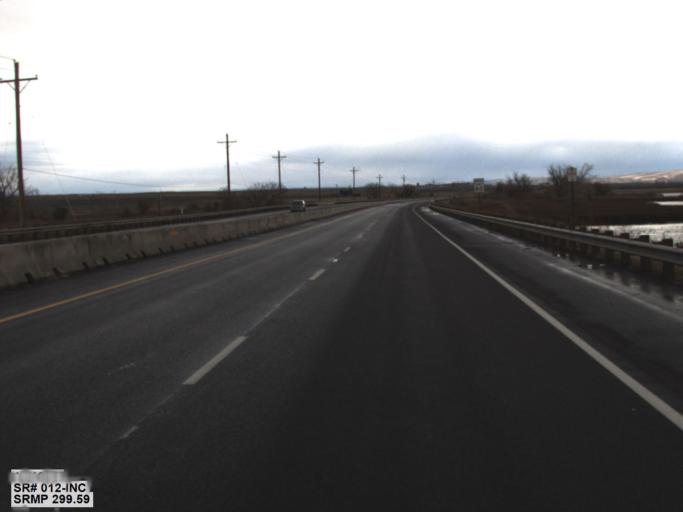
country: US
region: Washington
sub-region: Walla Walla County
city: Burbank
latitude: 46.1656
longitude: -118.9501
